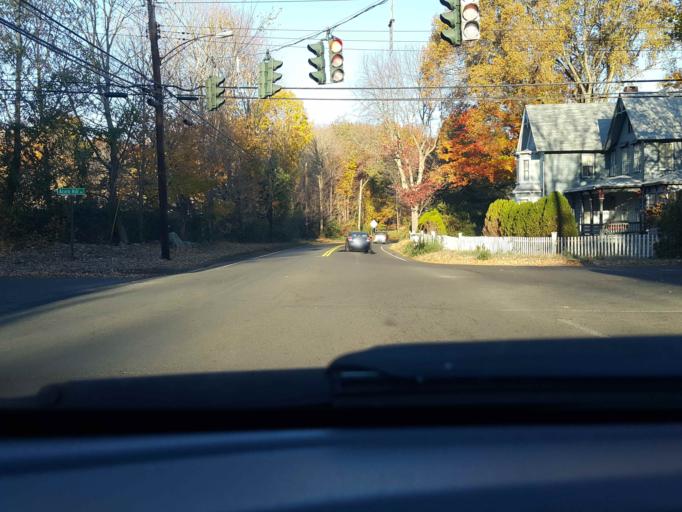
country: US
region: Connecticut
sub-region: New Haven County
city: Seymour
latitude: 41.3930
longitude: -73.0419
